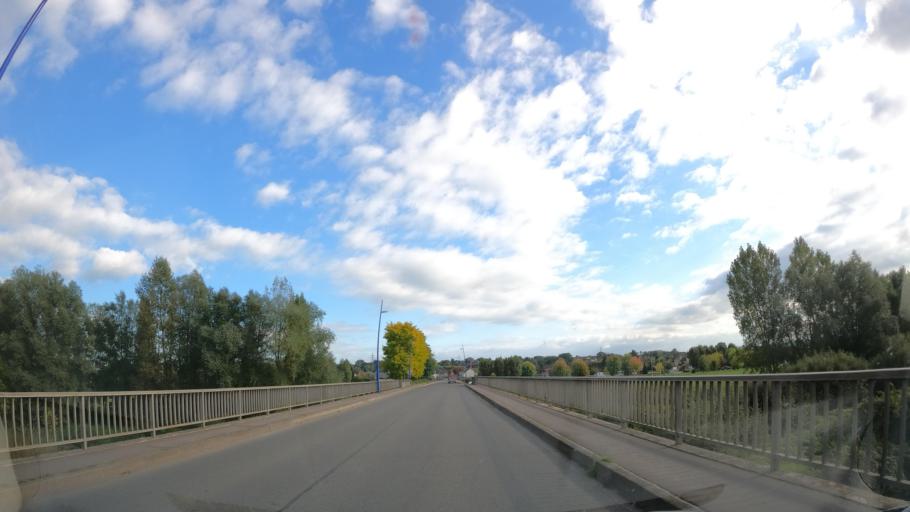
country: FR
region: Auvergne
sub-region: Departement de l'Allier
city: Dompierre-sur-Besbre
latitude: 46.5187
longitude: 3.6857
